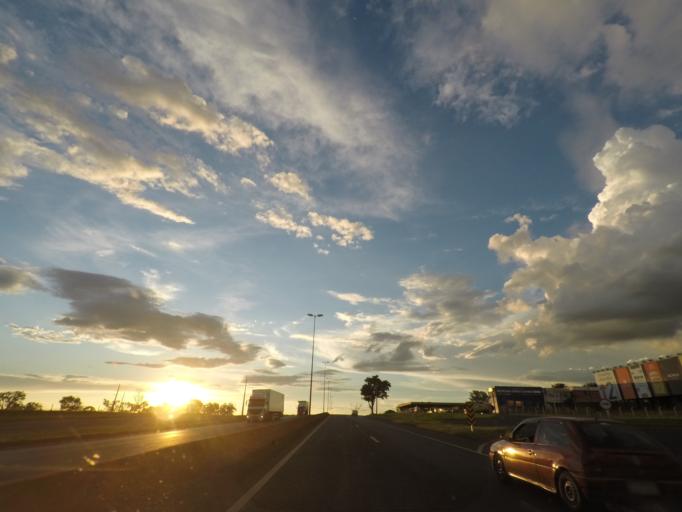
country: BR
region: Minas Gerais
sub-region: Uberaba
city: Uberaba
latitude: -19.7792
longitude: -47.9559
